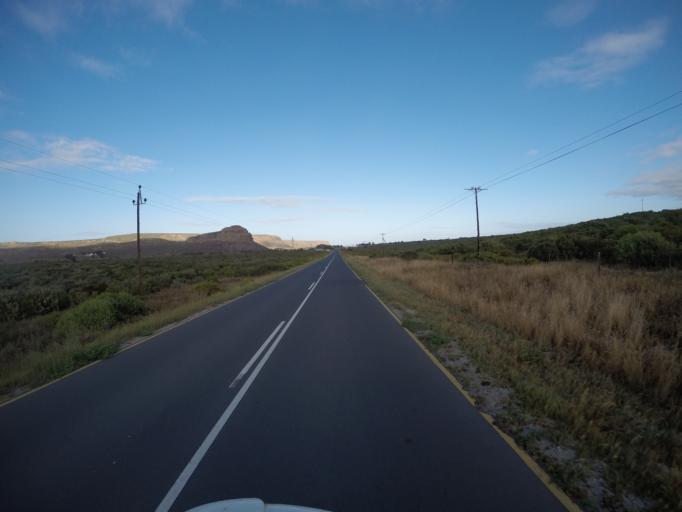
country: ZA
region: Western Cape
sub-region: West Coast District Municipality
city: Clanwilliam
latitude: -32.3126
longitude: 18.3675
